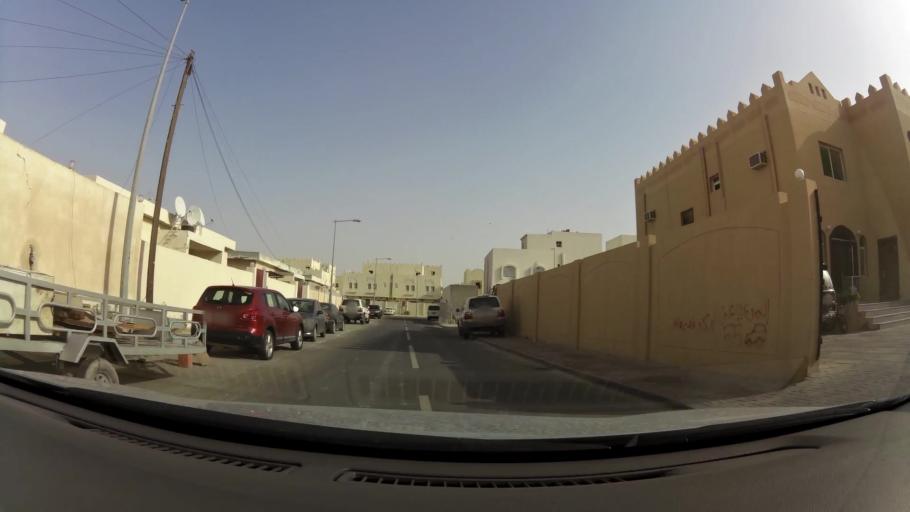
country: QA
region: Baladiyat ar Rayyan
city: Ar Rayyan
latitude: 25.2391
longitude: 51.4408
